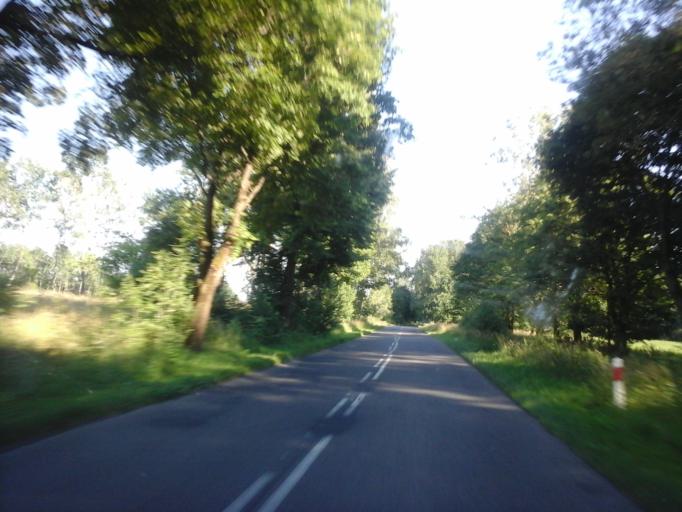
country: PL
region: West Pomeranian Voivodeship
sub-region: Powiat stargardzki
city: Chociwel
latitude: 53.4471
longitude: 15.3486
